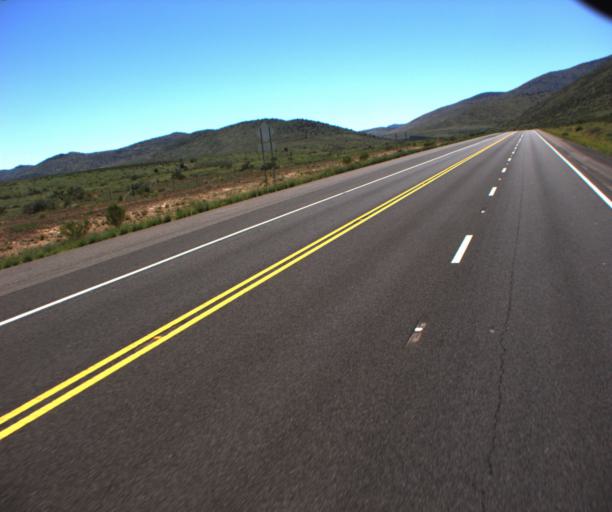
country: US
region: Arizona
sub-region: Greenlee County
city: Clifton
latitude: 32.9091
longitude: -109.2570
